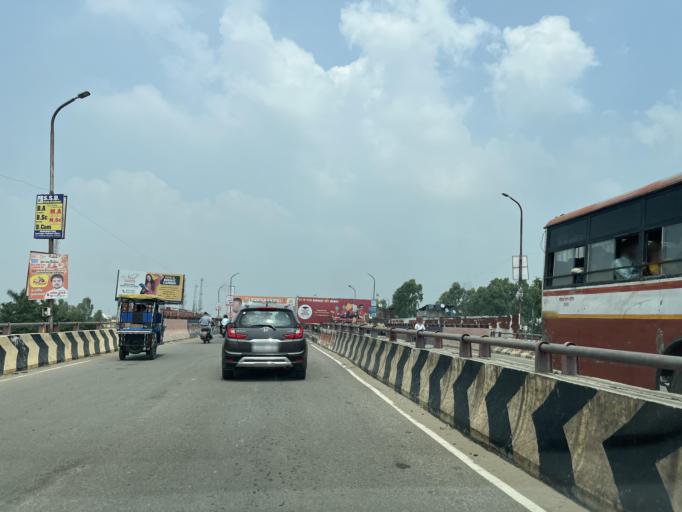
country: IN
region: Uttar Pradesh
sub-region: Bijnor
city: Najibabad
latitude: 29.6047
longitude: 78.3435
